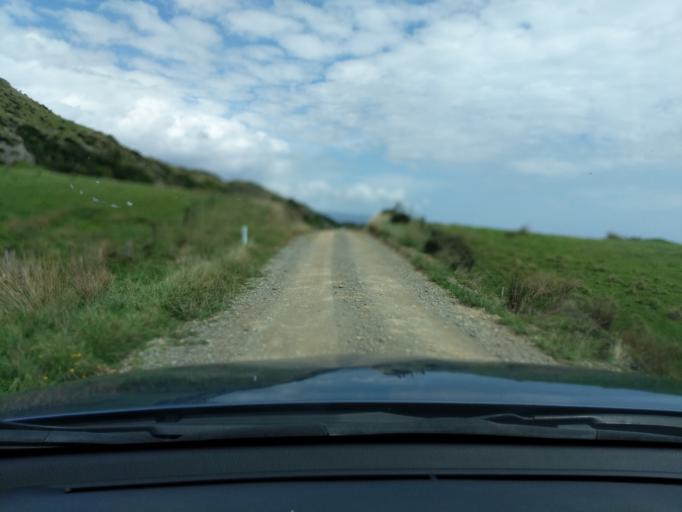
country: NZ
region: Tasman
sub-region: Tasman District
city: Takaka
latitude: -40.6629
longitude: 172.4106
